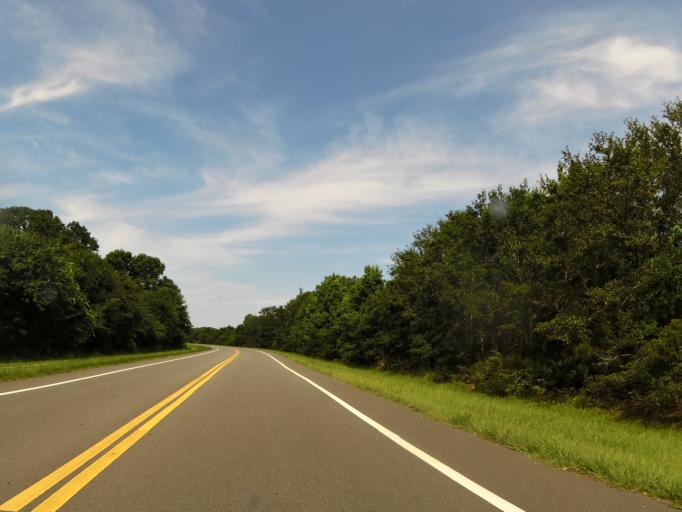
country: US
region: Florida
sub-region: Nassau County
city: Fernandina Beach
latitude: 30.6039
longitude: -81.4571
